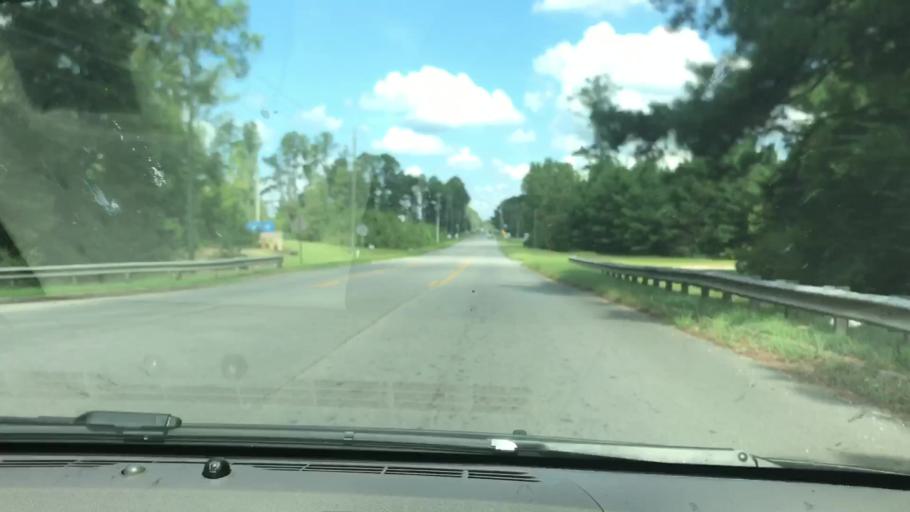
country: US
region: Georgia
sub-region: Troup County
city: La Grange
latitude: 32.9993
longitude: -85.0521
